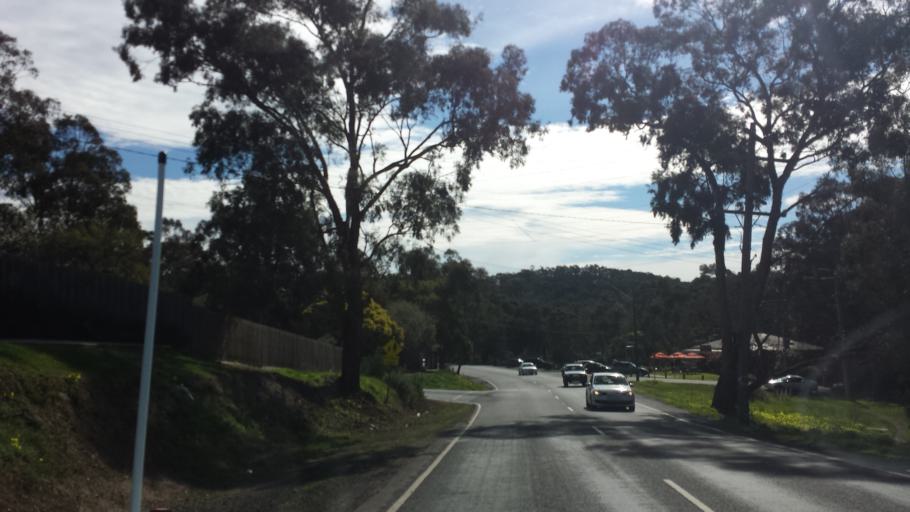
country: AU
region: Victoria
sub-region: Nillumbik
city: Wattleglen
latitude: -37.6676
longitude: 145.1841
